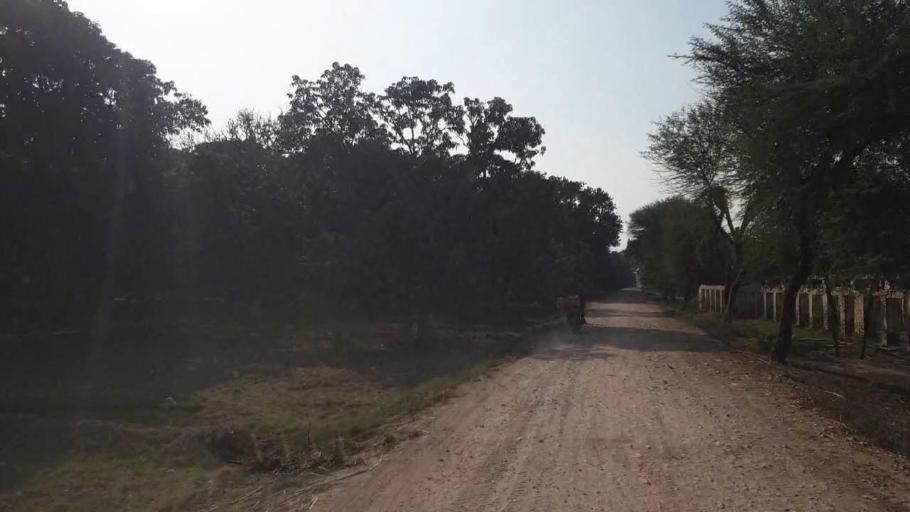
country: PK
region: Sindh
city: Mirpur Khas
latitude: 25.4128
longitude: 68.9497
